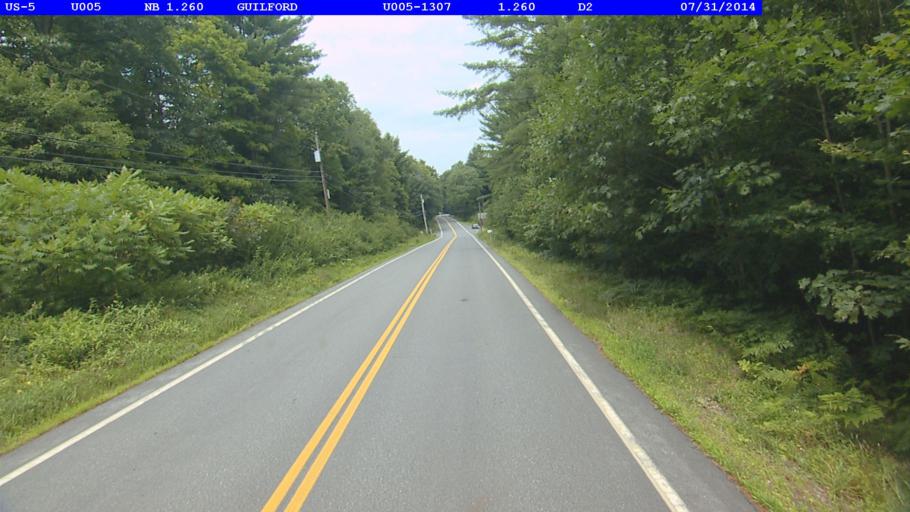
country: US
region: Massachusetts
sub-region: Franklin County
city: Bernardston
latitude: 42.7476
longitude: -72.5694
